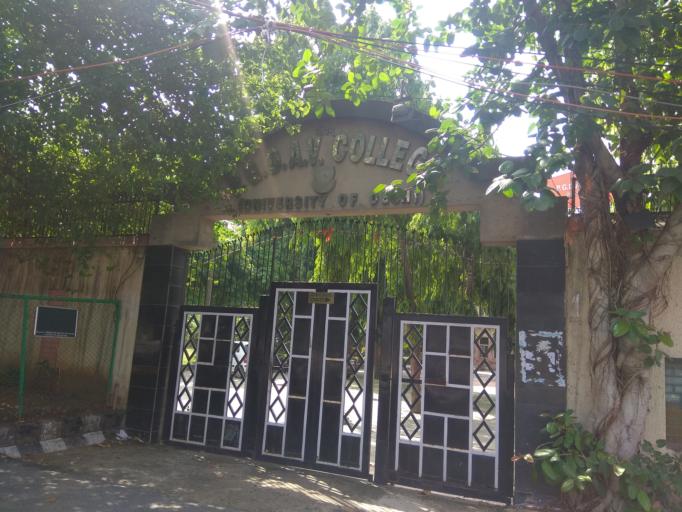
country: IN
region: NCT
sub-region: New Delhi
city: New Delhi
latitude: 28.5665
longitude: 77.2521
